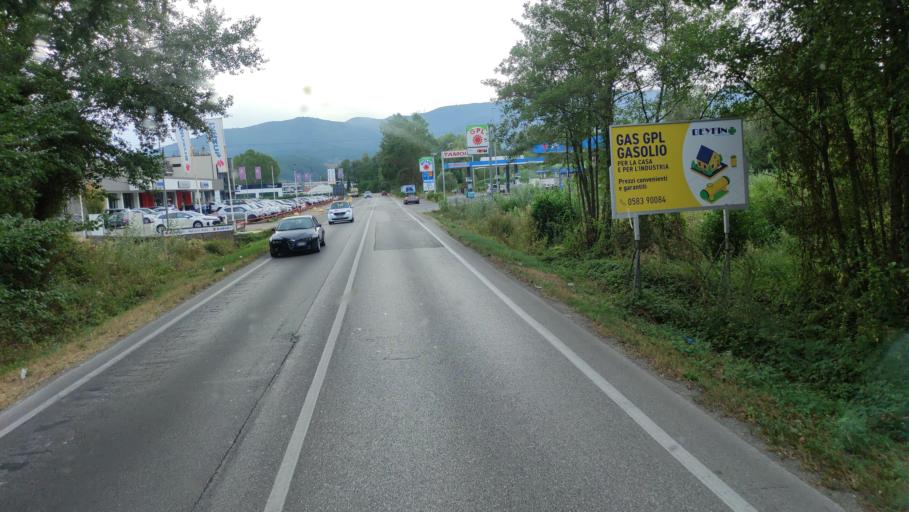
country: IT
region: Tuscany
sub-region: Provincia di Lucca
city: Lucca
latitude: 43.8184
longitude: 10.4928
